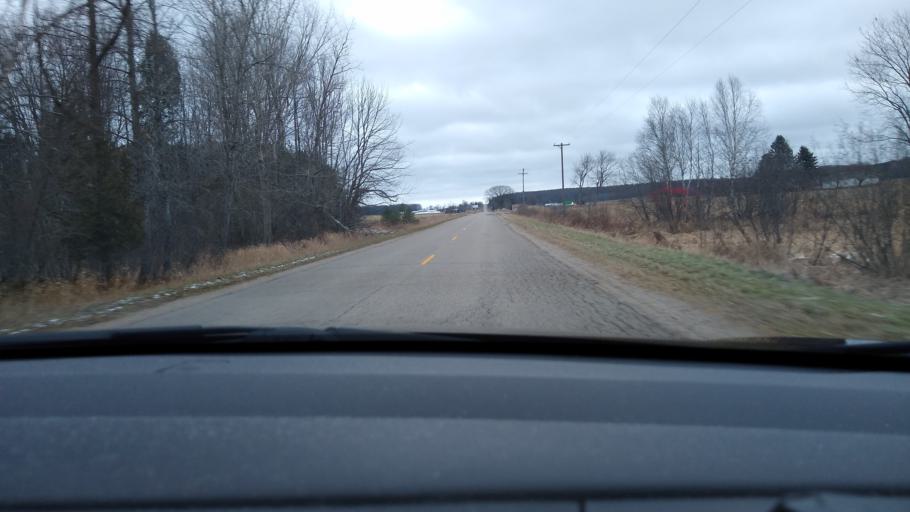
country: US
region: Michigan
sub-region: Missaukee County
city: Lake City
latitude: 44.2700
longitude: -85.0540
